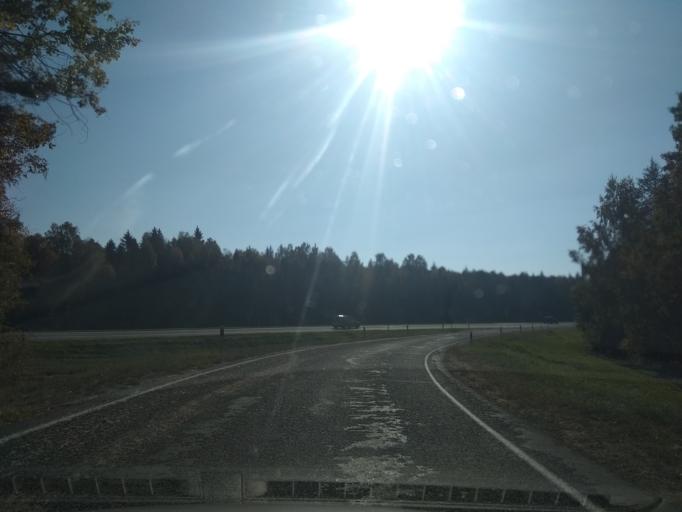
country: BY
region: Brest
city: Ivatsevichy
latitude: 52.8538
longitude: 25.6425
